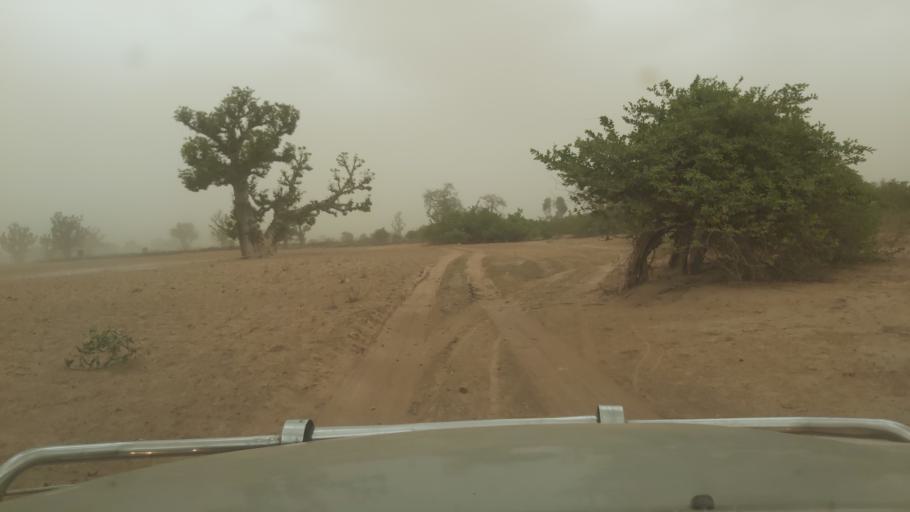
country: ML
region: Koulikoro
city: Banamba
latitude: 13.3775
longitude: -7.2045
